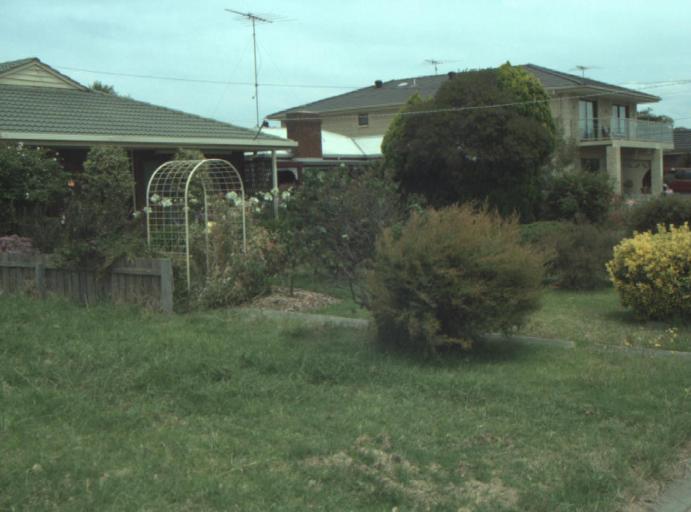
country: AU
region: Victoria
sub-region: Greater Geelong
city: Clifton Springs
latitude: -38.1571
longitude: 144.5541
